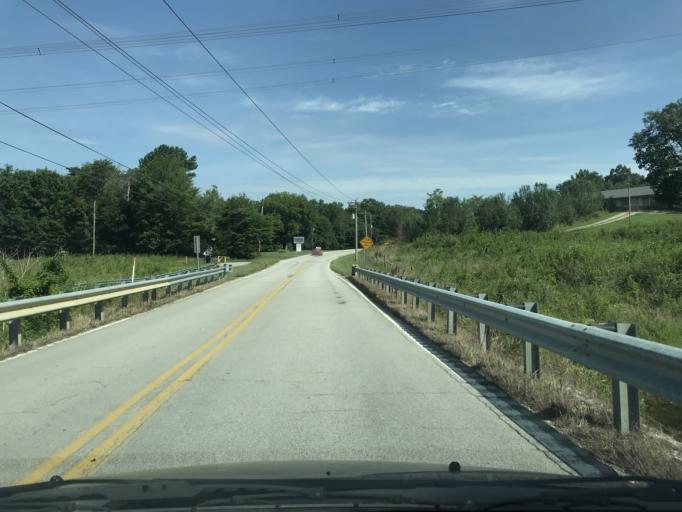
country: US
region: Tennessee
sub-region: Hamilton County
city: Lakesite
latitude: 35.2515
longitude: -85.0675
